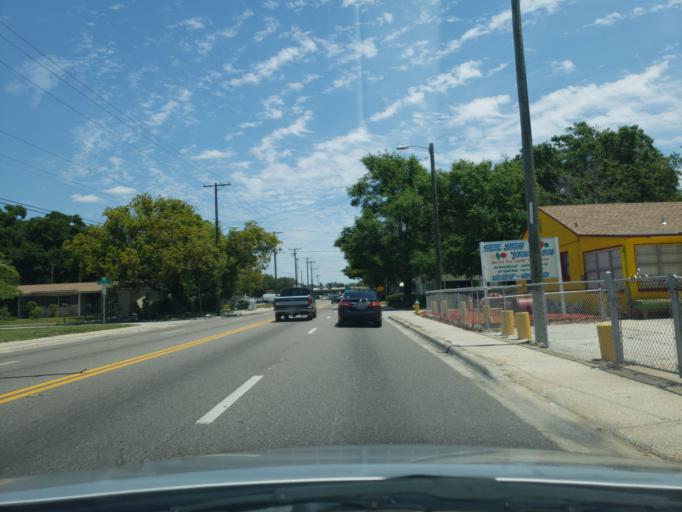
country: US
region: Florida
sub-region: Hillsborough County
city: Egypt Lake-Leto
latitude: 28.0106
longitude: -82.4574
